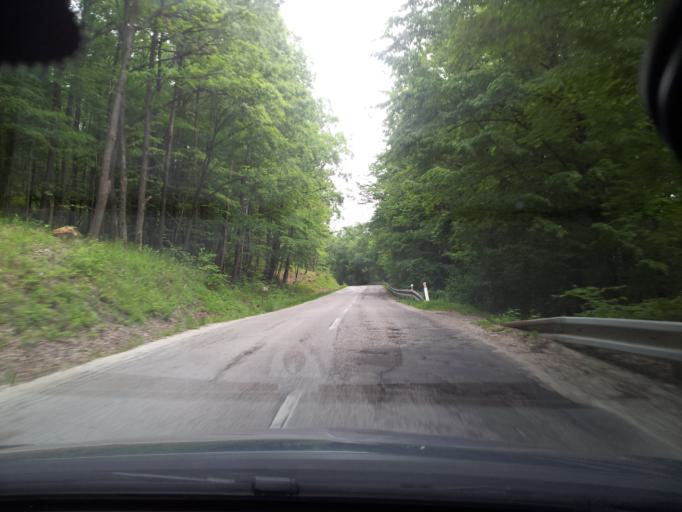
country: SK
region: Nitriansky
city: Partizanske
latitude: 48.5572
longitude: 18.4523
